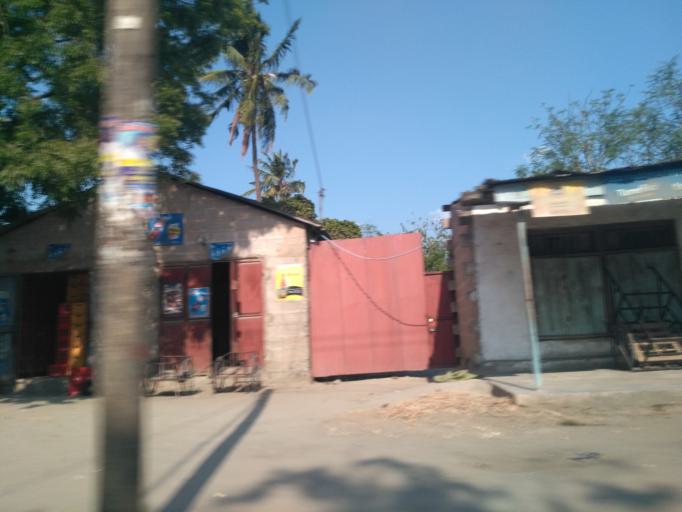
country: TZ
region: Dar es Salaam
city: Dar es Salaam
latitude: -6.8619
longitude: 39.3105
